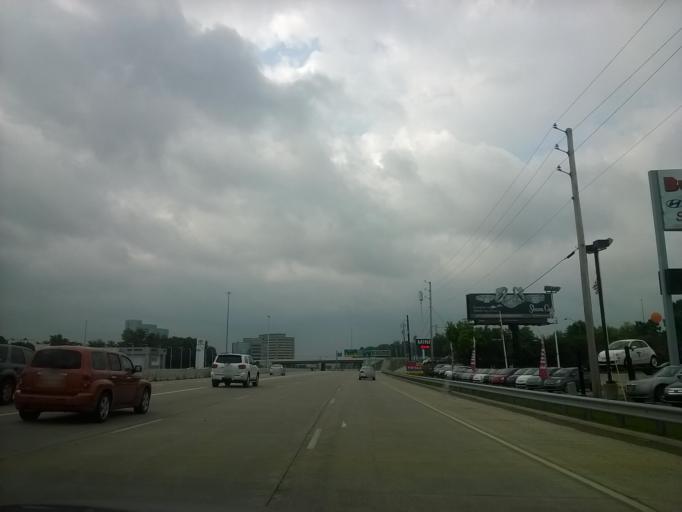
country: US
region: Indiana
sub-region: Hamilton County
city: Carmel
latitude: 39.9255
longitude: -86.1125
